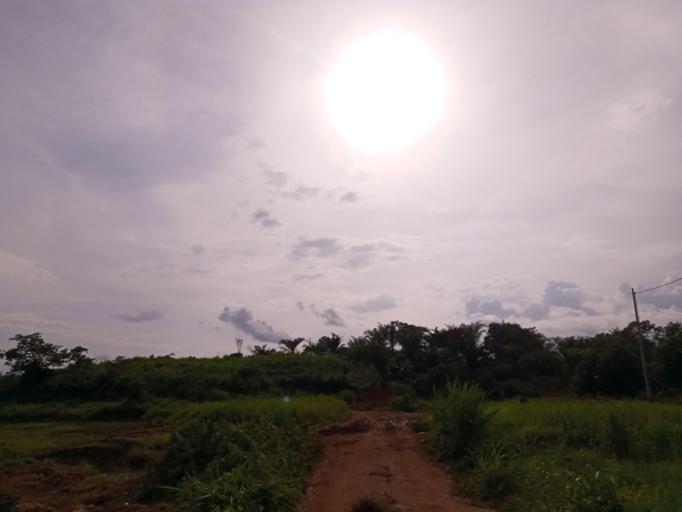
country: SL
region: Northern Province
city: Bumbuna
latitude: 9.0457
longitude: -11.7577
